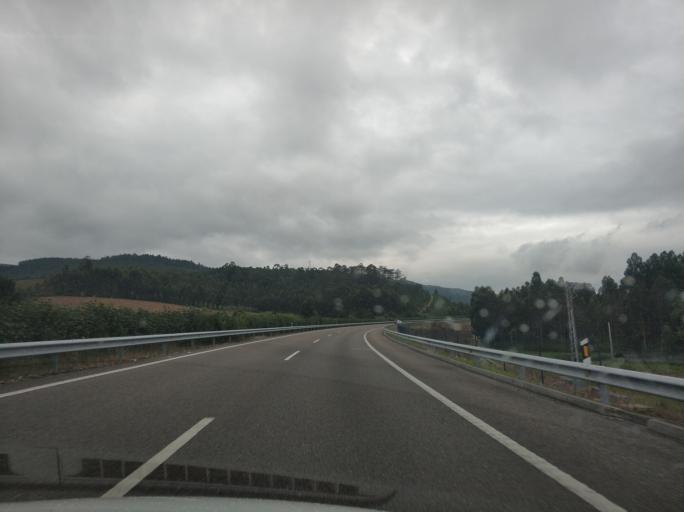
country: ES
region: Galicia
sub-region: Provincia de Lugo
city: Ribadeo
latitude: 43.5376
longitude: -7.0827
